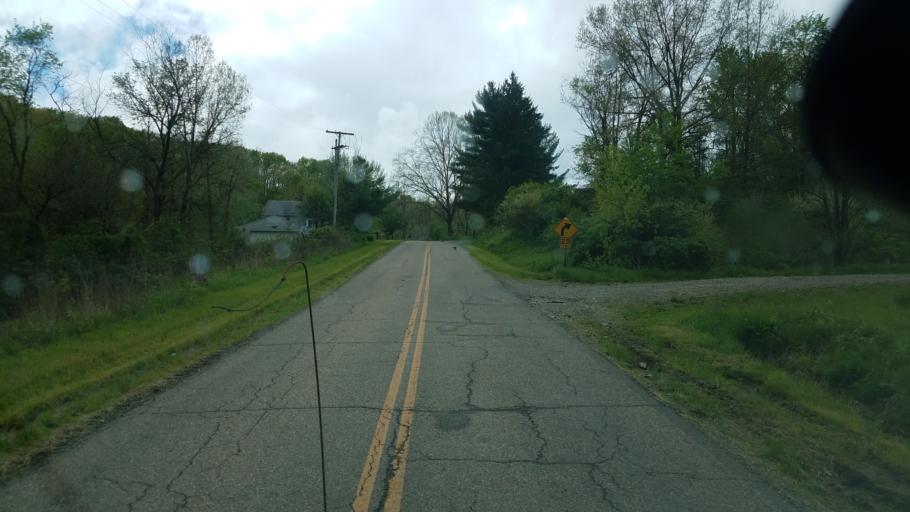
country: US
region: Ohio
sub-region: Harrison County
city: Cadiz
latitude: 40.2712
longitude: -80.9293
